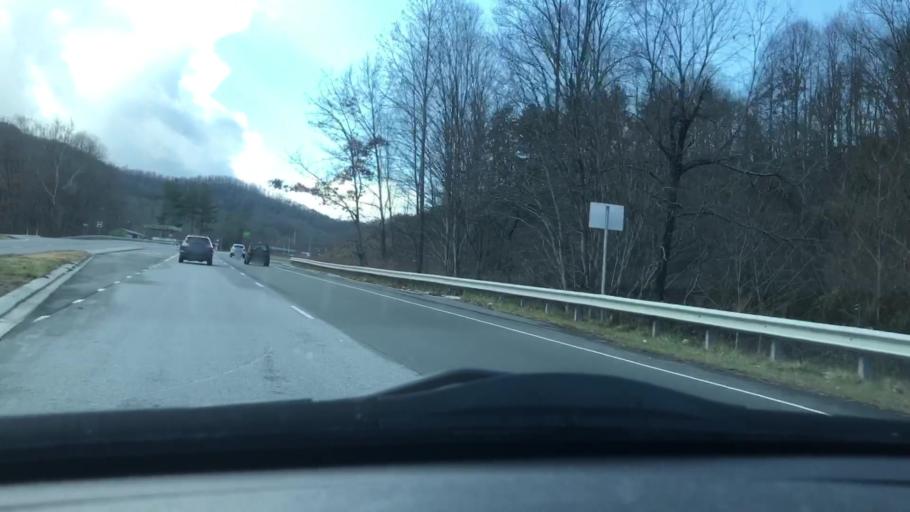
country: US
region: North Carolina
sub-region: Yancey County
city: Burnsville
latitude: 35.9143
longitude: -82.2530
